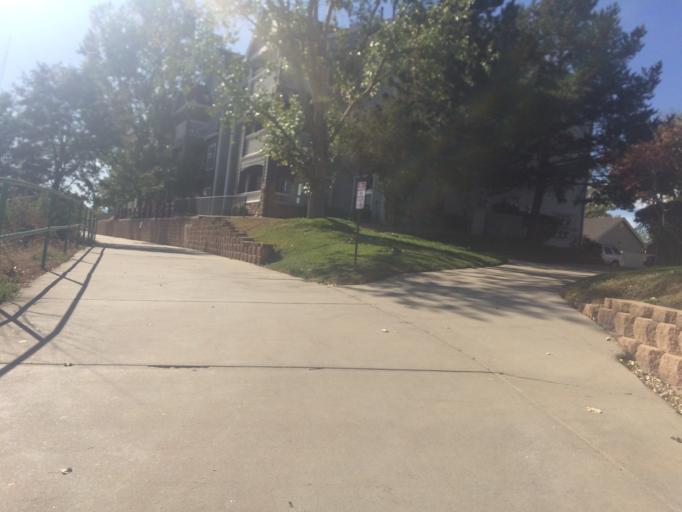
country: US
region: Colorado
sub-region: Broomfield County
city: Broomfield
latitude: 39.8790
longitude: -105.0785
